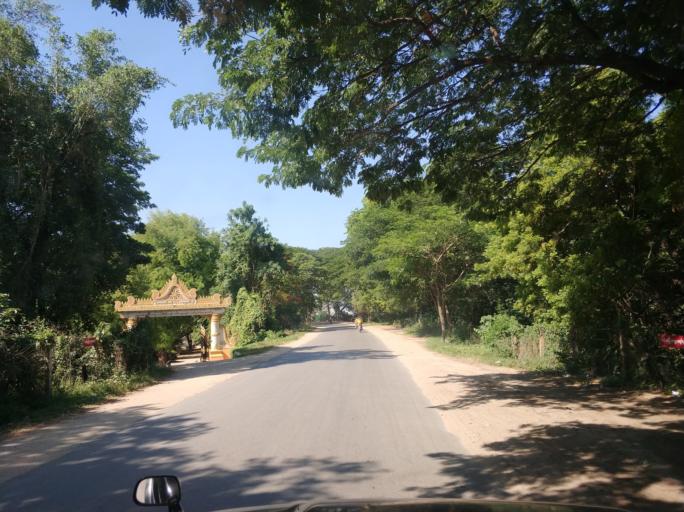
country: MM
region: Mandalay
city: Mandalay
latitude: 21.9547
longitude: 96.0516
